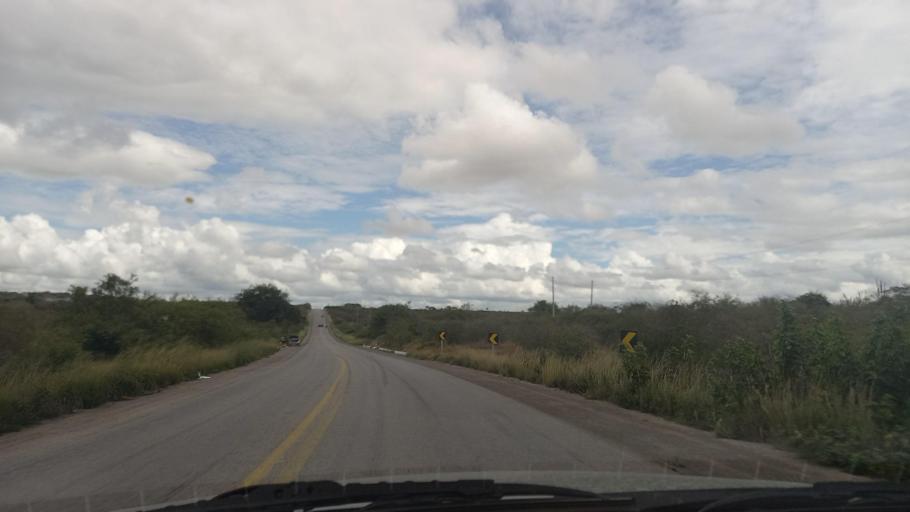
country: BR
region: Pernambuco
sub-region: Cachoeirinha
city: Cachoeirinha
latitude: -8.3537
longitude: -36.1718
